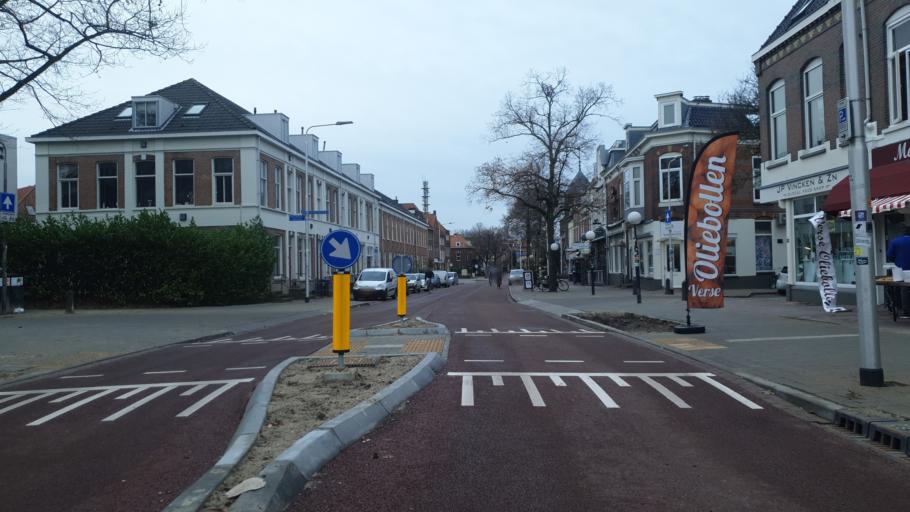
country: NL
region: Gelderland
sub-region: Gemeente Nijmegen
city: Nijmegen
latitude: 51.8409
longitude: 5.8715
